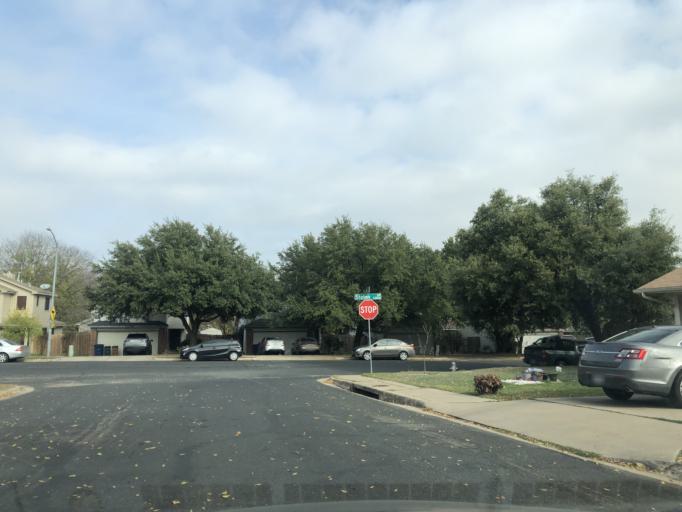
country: US
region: Texas
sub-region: Travis County
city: Wells Branch
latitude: 30.4200
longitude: -97.6858
